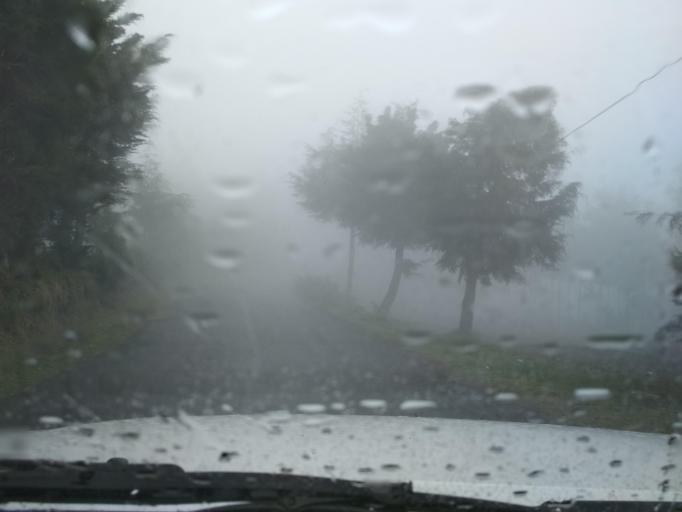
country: MX
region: Veracruz
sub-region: Mariano Escobedo
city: San Isidro el Berro
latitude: 18.9305
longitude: -97.2129
